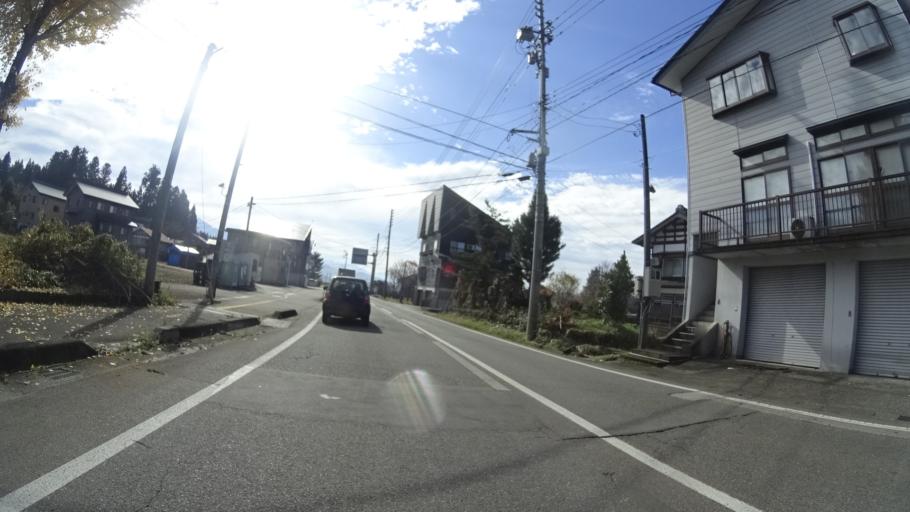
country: JP
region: Niigata
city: Ojiya
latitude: 37.2559
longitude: 138.9816
